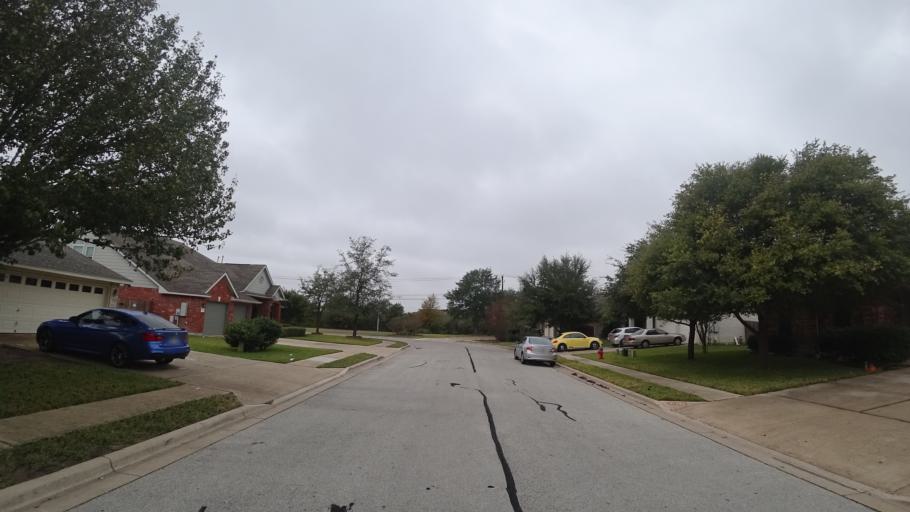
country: US
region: Texas
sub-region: Travis County
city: Pflugerville
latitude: 30.4293
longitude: -97.6189
